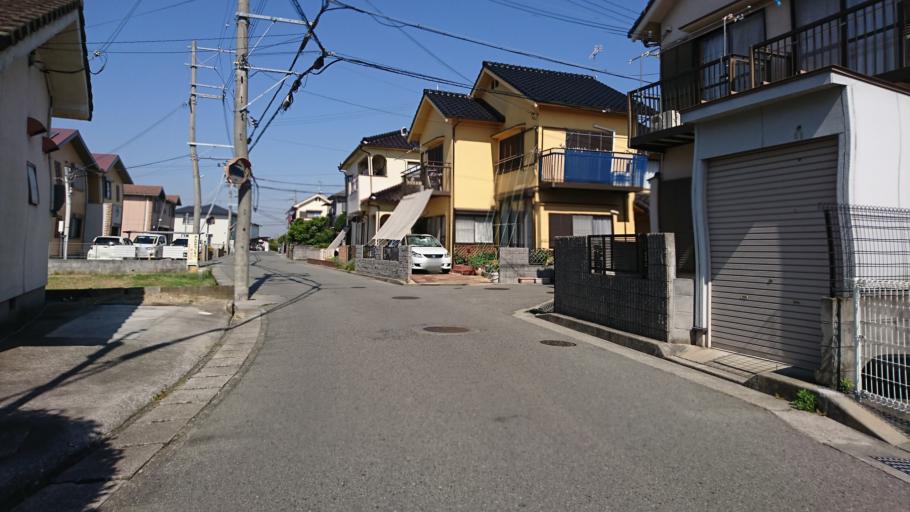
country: JP
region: Hyogo
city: Kakogawacho-honmachi
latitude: 34.7574
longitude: 134.8777
